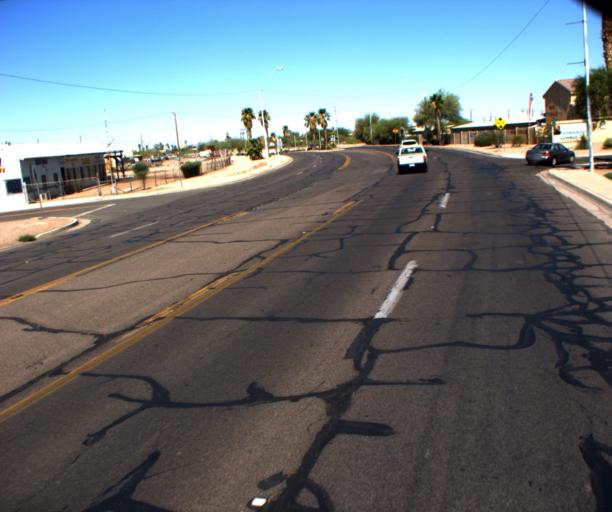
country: US
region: Arizona
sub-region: Pinal County
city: Casa Grande
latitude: 32.8802
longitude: -111.7590
